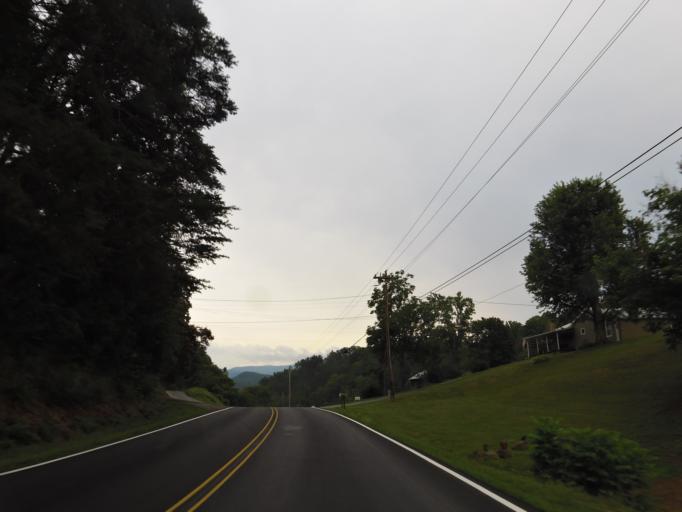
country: US
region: Tennessee
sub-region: Sevier County
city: Pigeon Forge
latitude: 35.8023
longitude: -83.6242
